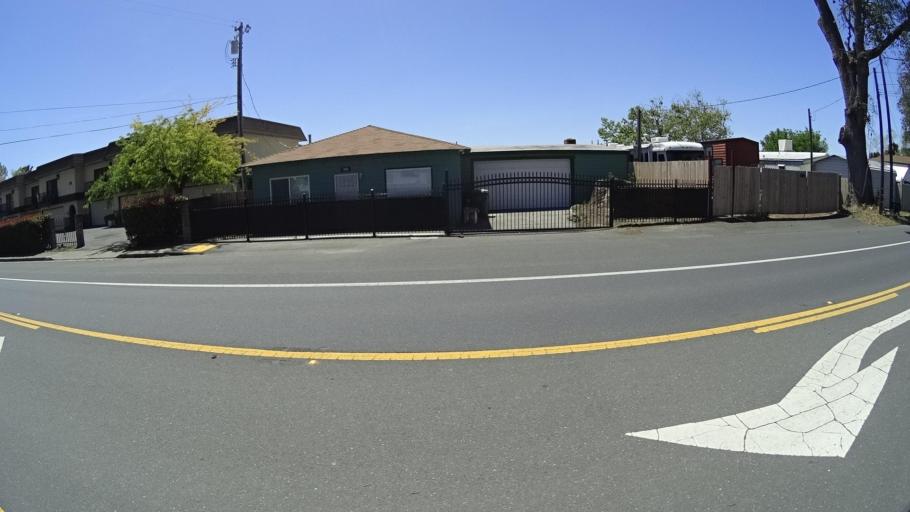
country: US
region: California
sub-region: Lake County
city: Lucerne
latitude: 39.0886
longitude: -122.7943
